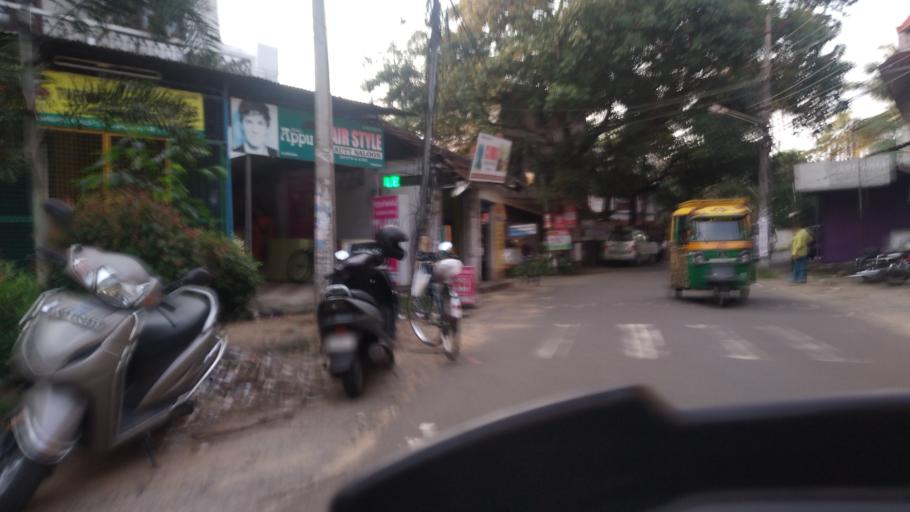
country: IN
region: Kerala
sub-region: Ernakulam
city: Elur
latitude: 10.0247
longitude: 76.2987
